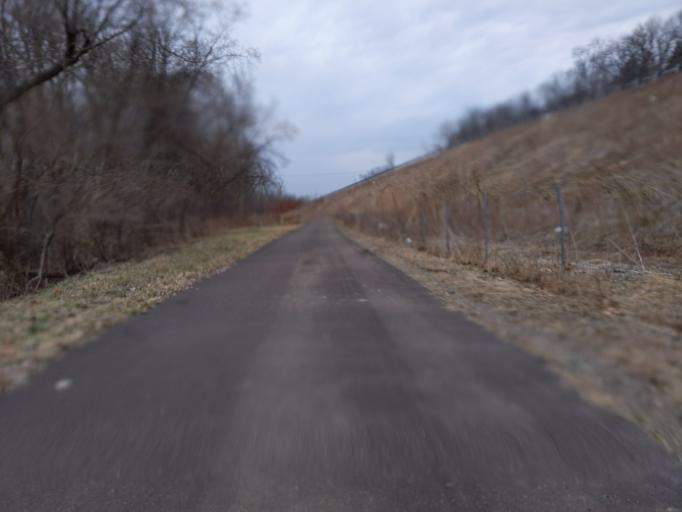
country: US
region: New York
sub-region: Chemung County
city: Elmira
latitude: 42.0561
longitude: -76.7553
